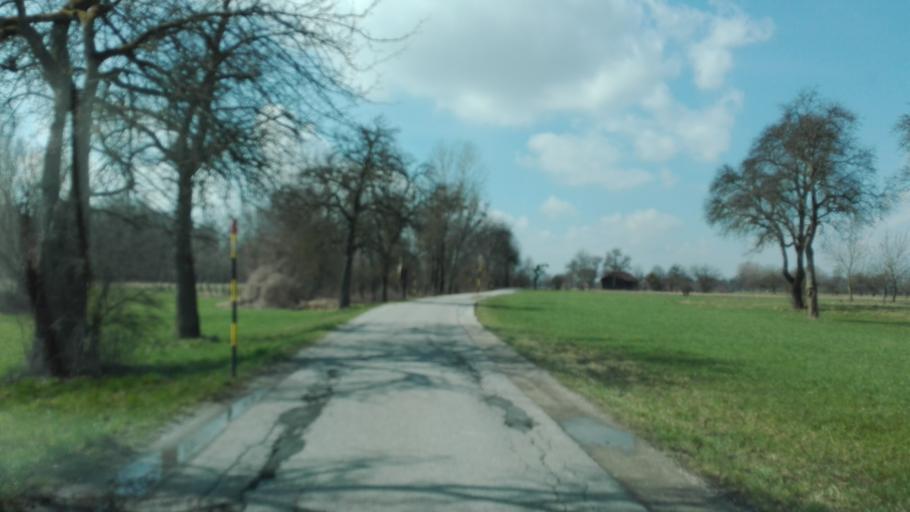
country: AT
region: Upper Austria
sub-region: Politischer Bezirk Urfahr-Umgebung
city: Ottensheim
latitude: 48.3289
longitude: 14.1577
